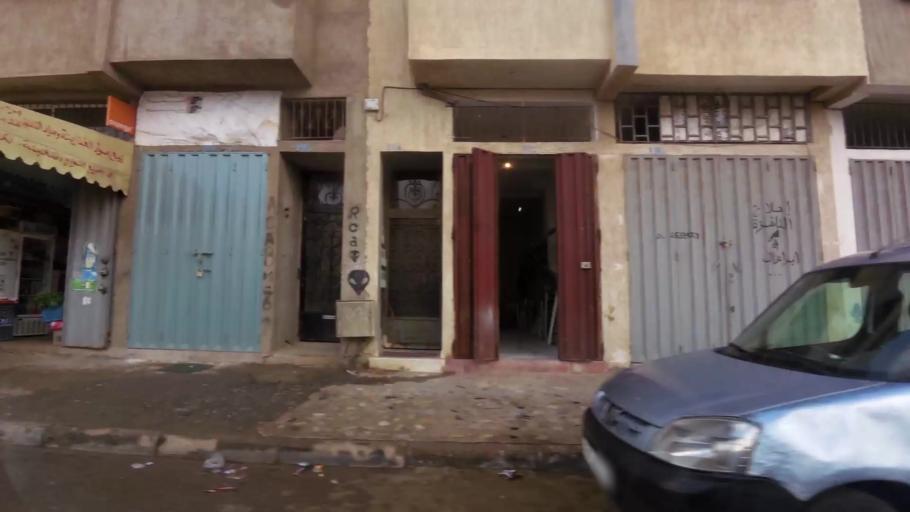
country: MA
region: Grand Casablanca
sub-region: Nouaceur
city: Bouskoura
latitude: 33.5360
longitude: -7.7054
